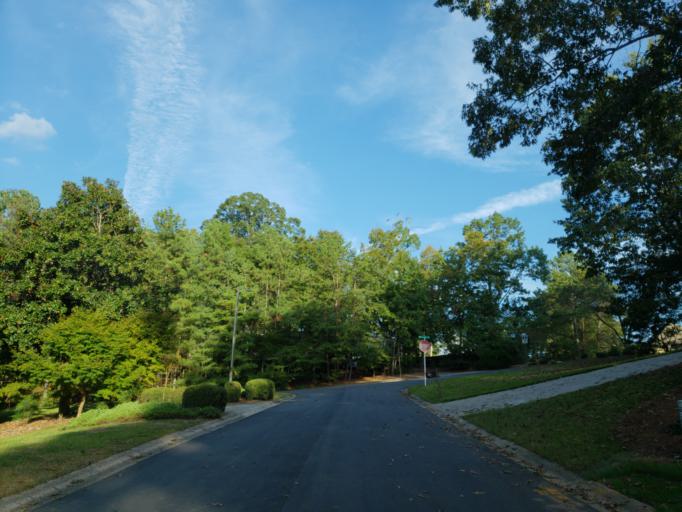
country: US
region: Georgia
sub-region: Fulton County
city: Roswell
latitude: 34.0449
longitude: -84.4356
